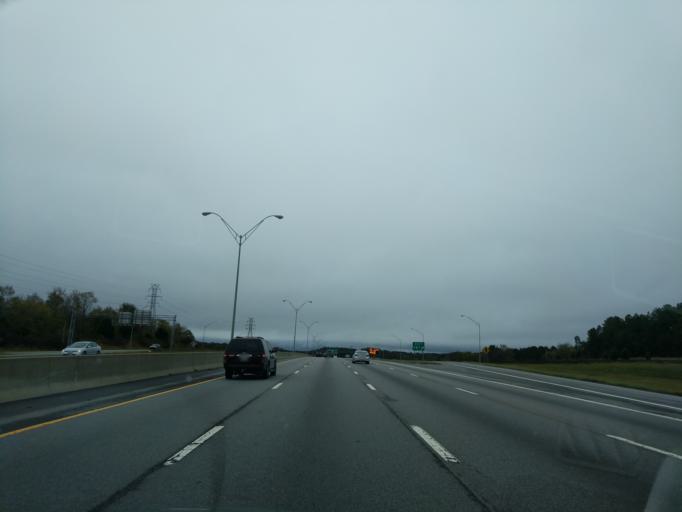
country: US
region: North Carolina
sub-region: Orange County
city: Hillsborough
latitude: 36.0734
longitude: -79.1692
